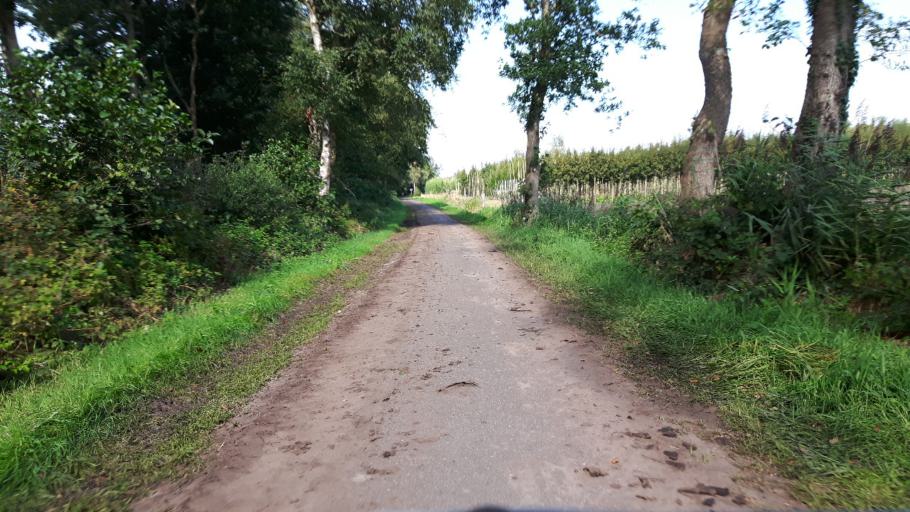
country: NL
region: Groningen
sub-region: Gemeente Leek
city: Leek
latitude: 53.1216
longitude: 6.4675
